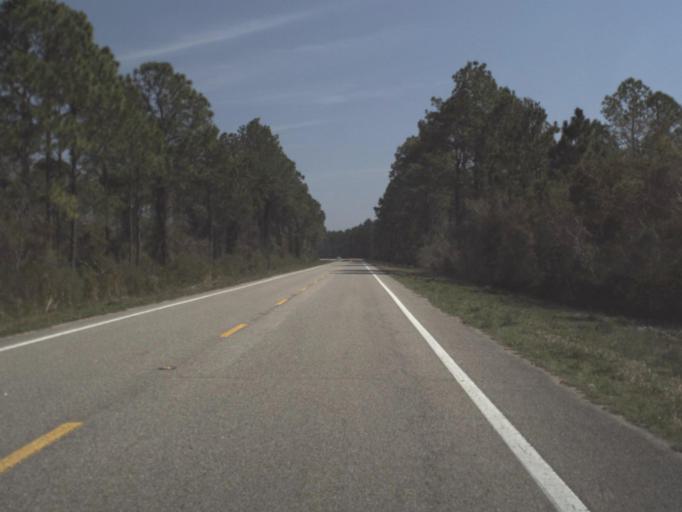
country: US
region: Florida
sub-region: Gulf County
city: Port Saint Joe
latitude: 29.7441
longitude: -85.2326
